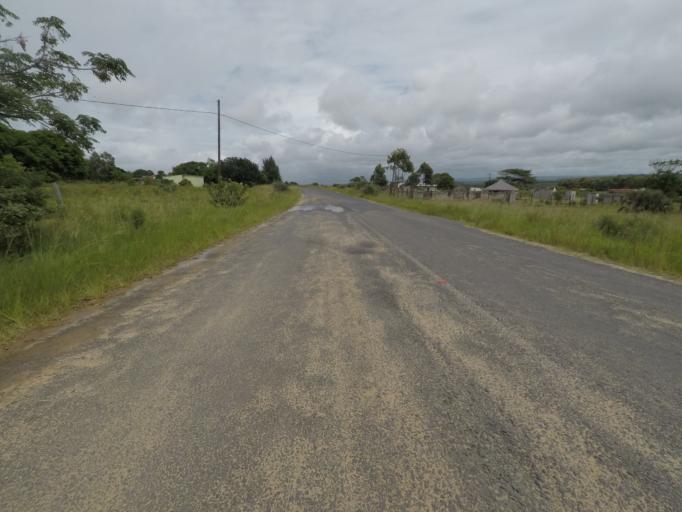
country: ZA
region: KwaZulu-Natal
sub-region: uThungulu District Municipality
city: eSikhawini
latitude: -28.9128
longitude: 31.8567
